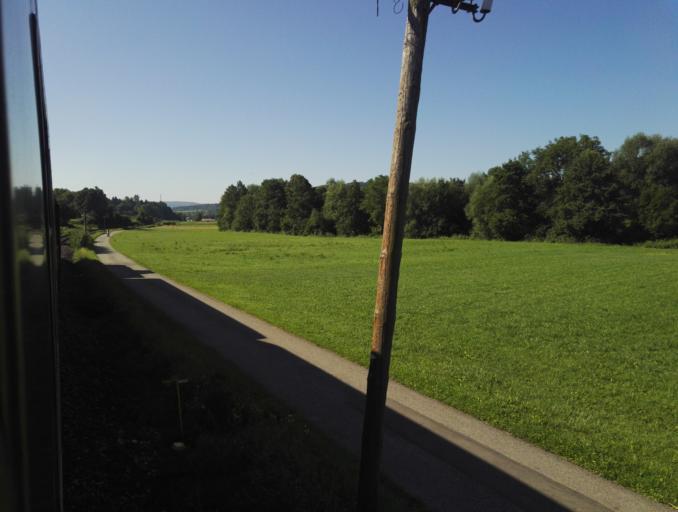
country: DE
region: Baden-Wuerttemberg
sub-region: Regierungsbezirk Stuttgart
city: Rudersberg
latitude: 48.8568
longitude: 9.5377
